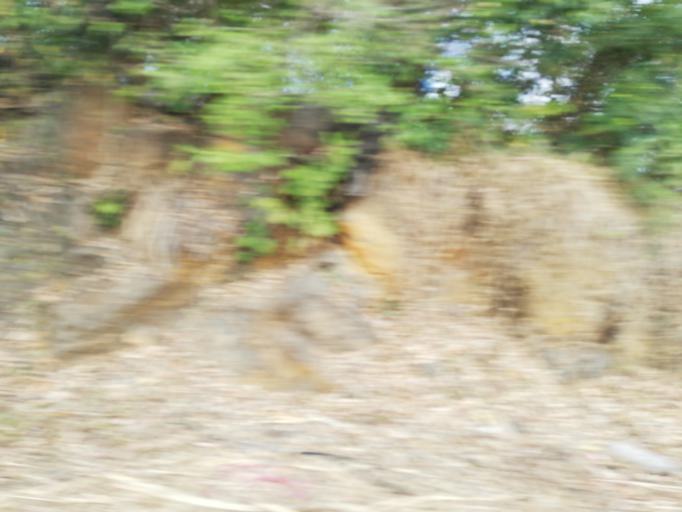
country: MU
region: Flacq
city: Grande Riviere Sud Est
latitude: -20.2740
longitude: 57.7685
